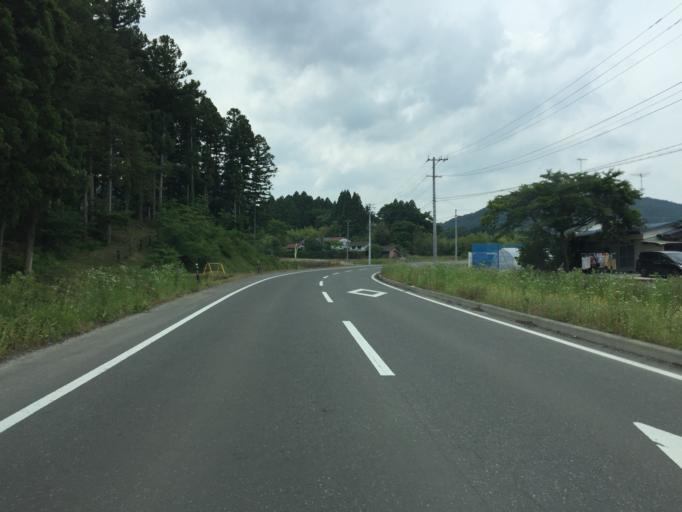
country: JP
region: Miyagi
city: Marumori
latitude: 37.8179
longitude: 140.8874
